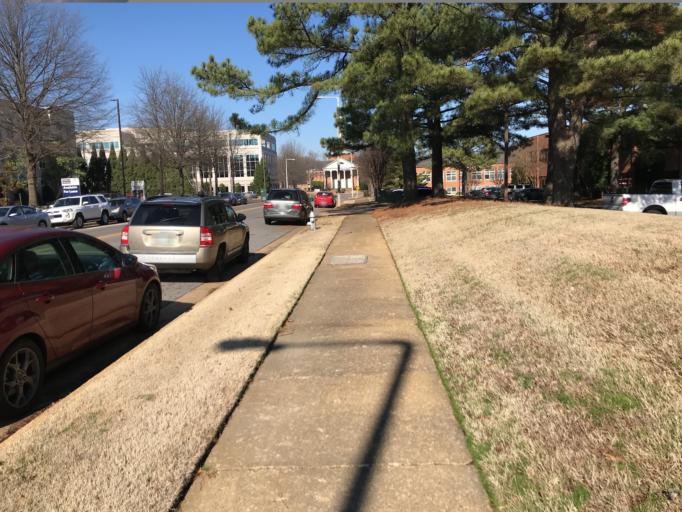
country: US
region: Tennessee
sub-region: Shelby County
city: Germantown
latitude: 35.1096
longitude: -89.8678
